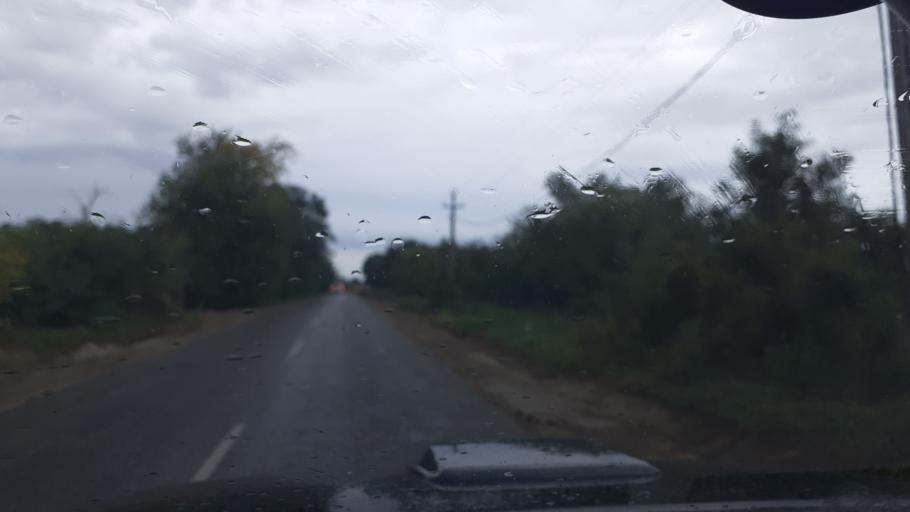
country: HU
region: Tolna
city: Bolcske
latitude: 46.7538
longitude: 18.9636
